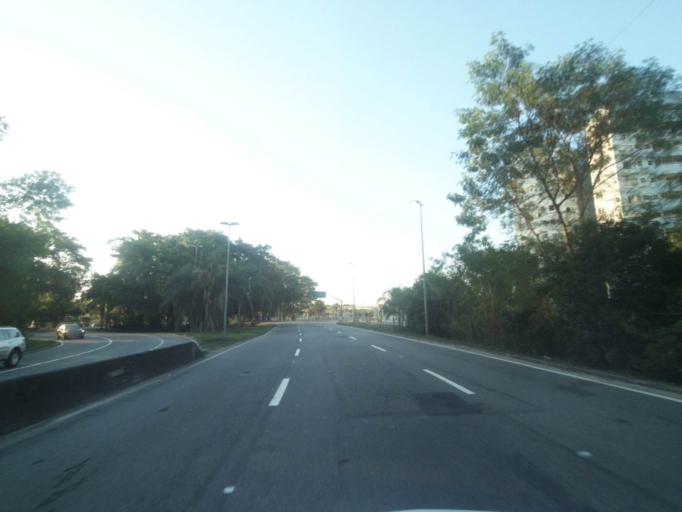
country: BR
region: Rio de Janeiro
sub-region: Rio De Janeiro
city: Rio de Janeiro
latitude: -22.9728
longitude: -43.3608
